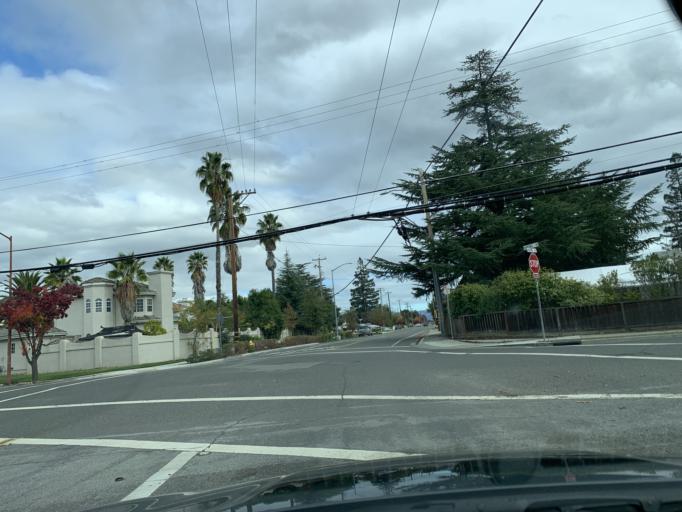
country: US
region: California
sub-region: Santa Clara County
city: Campbell
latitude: 37.2691
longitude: -121.9725
